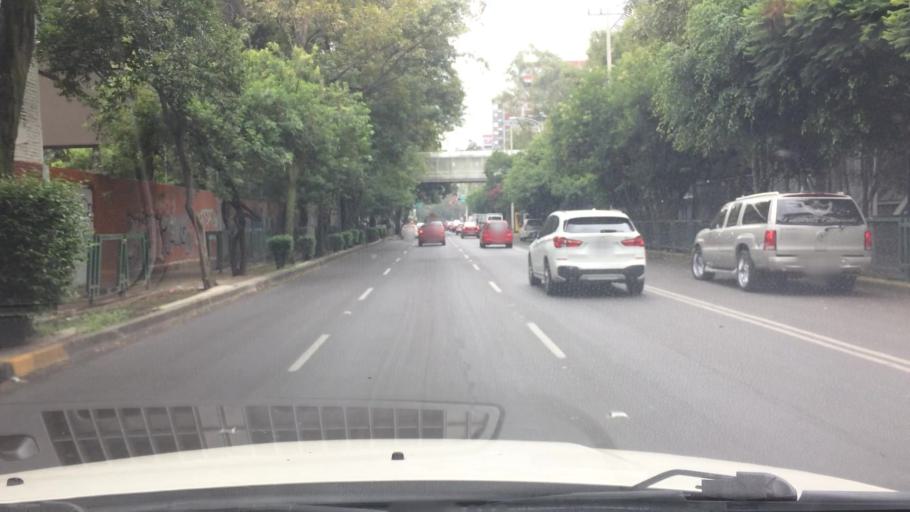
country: MX
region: Mexico City
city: Colonia del Valle
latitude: 19.3736
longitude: -99.1705
